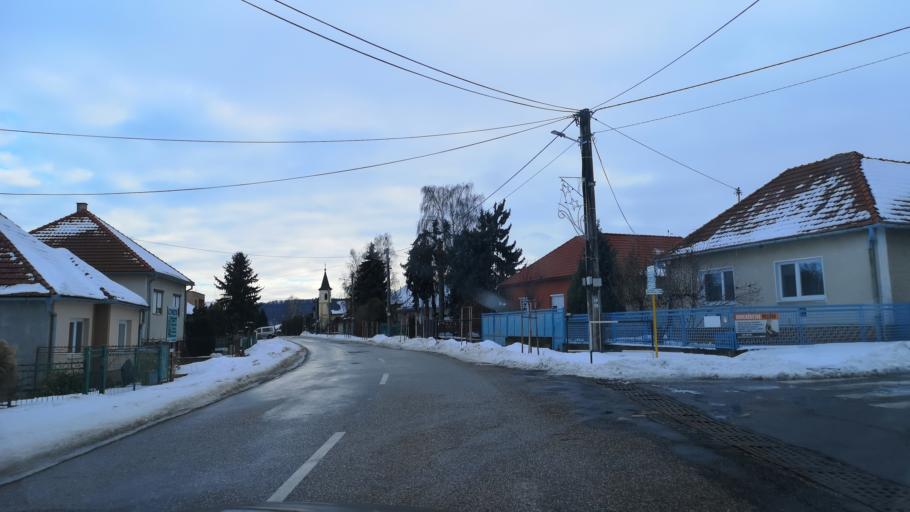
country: SK
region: Nitriansky
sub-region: Okres Nitra
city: Vrable
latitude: 48.1135
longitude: 18.3358
